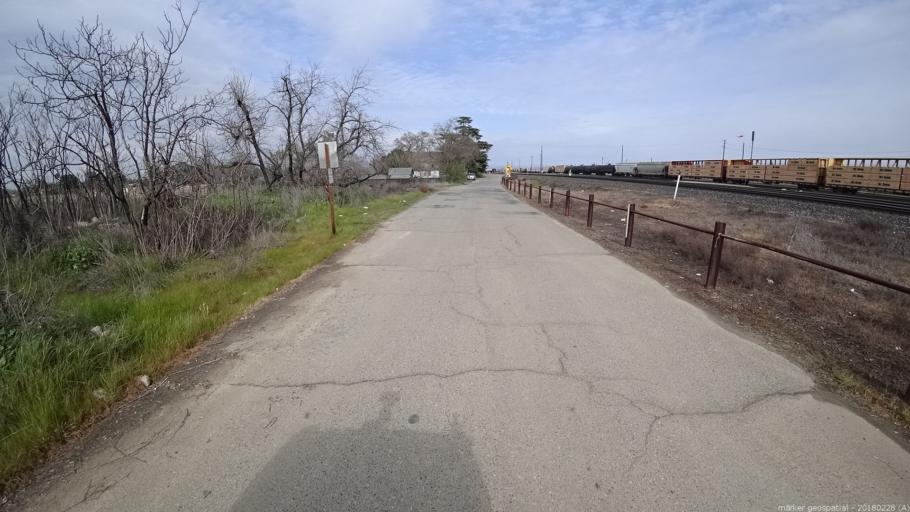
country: US
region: California
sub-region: Sacramento County
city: Antelope
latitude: 38.7075
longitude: -121.3311
